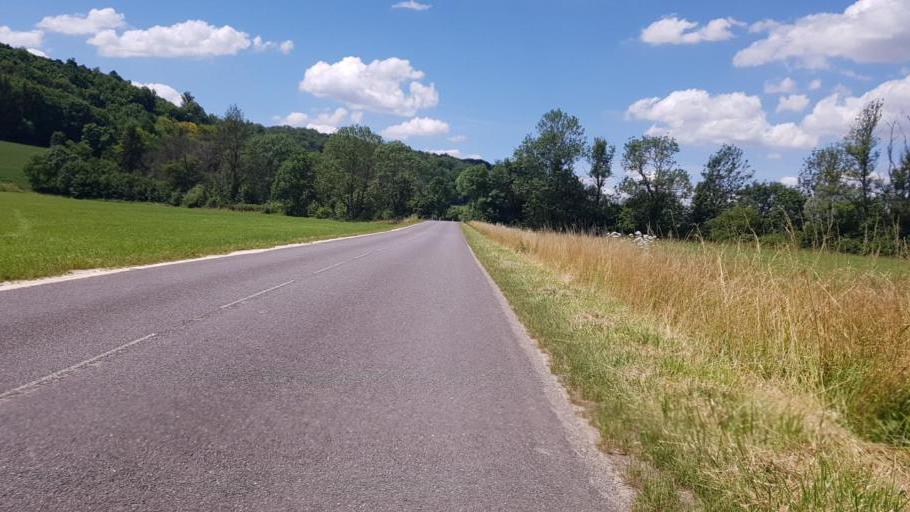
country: FR
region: Lorraine
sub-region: Departement de la Meuse
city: Ligny-en-Barrois
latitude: 48.6417
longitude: 5.4407
